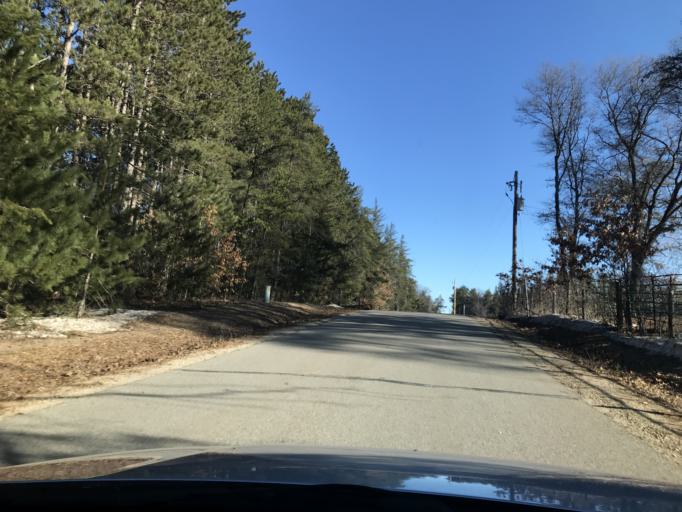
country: US
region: Wisconsin
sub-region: Marinette County
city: Niagara
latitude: 45.3961
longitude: -88.0791
